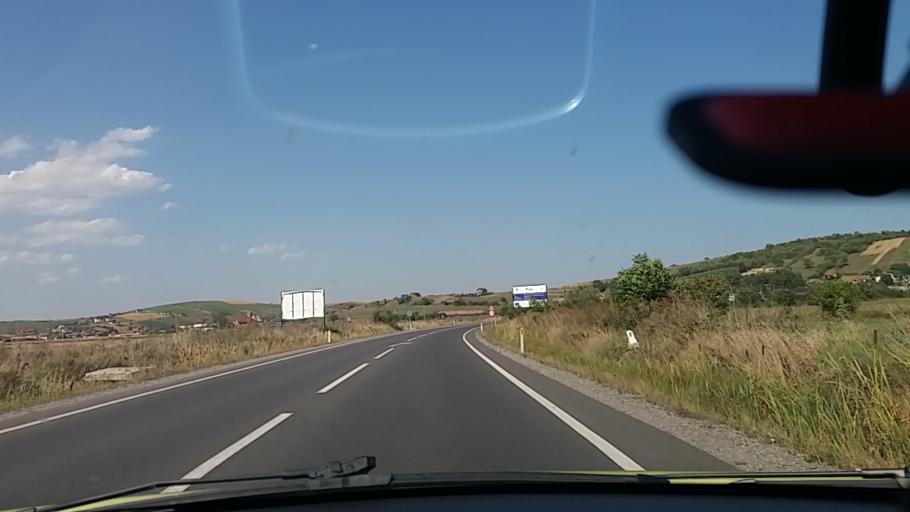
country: RO
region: Sibiu
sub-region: Comuna Sura Mare
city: Sura Mare
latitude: 45.8331
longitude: 24.1525
